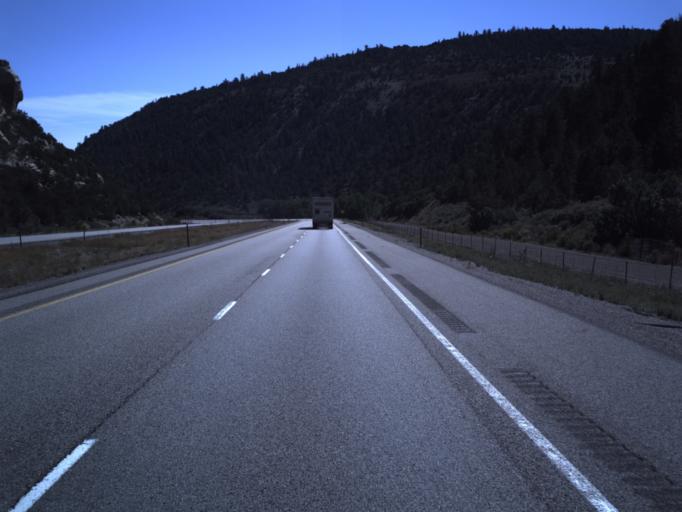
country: US
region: Utah
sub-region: Wayne County
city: Loa
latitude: 38.7586
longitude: -111.4495
